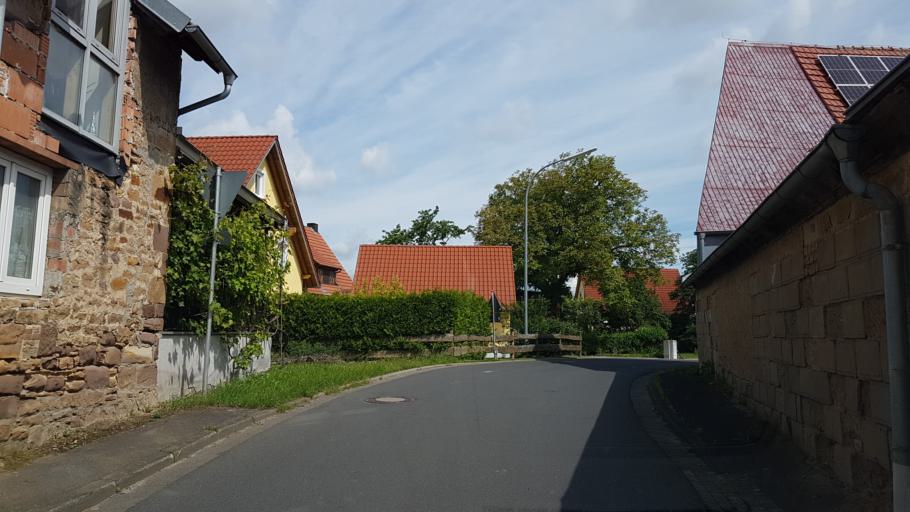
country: DE
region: Bavaria
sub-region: Regierungsbezirk Unterfranken
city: Lulsfeld
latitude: 49.8524
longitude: 10.3279
